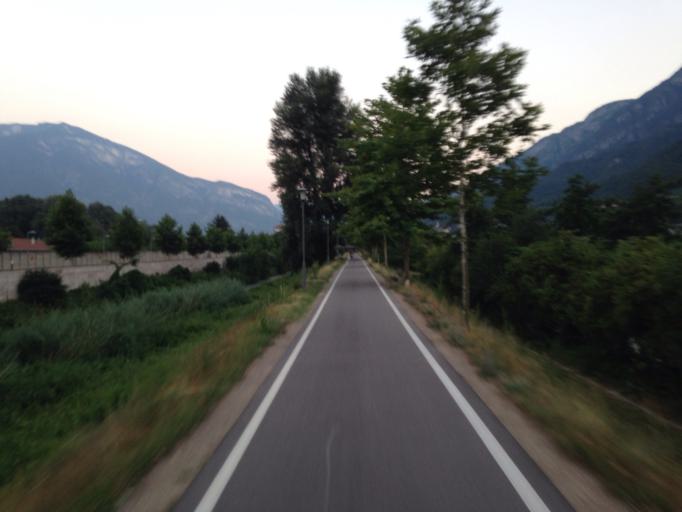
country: IT
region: Trentino-Alto Adige
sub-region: Provincia di Trento
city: Trento
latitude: 46.0558
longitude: 11.1119
